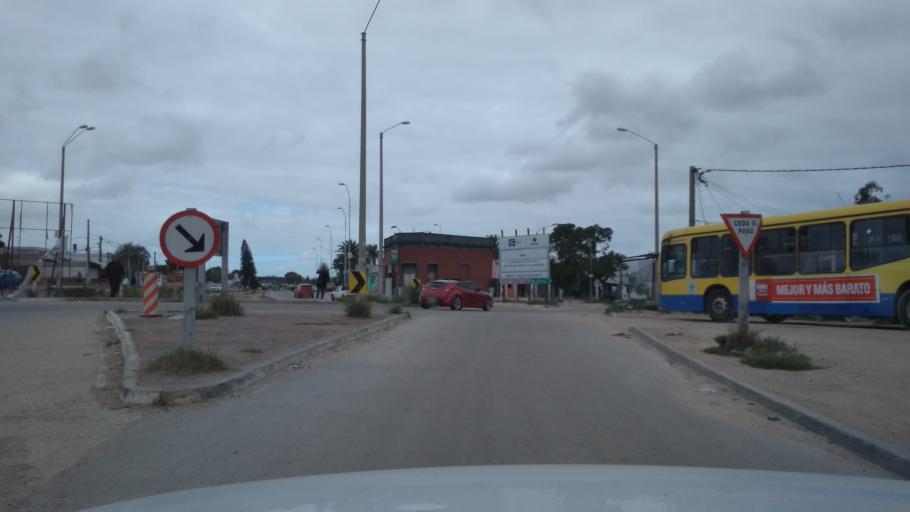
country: UY
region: Canelones
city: Toledo
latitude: -34.7808
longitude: -56.1365
